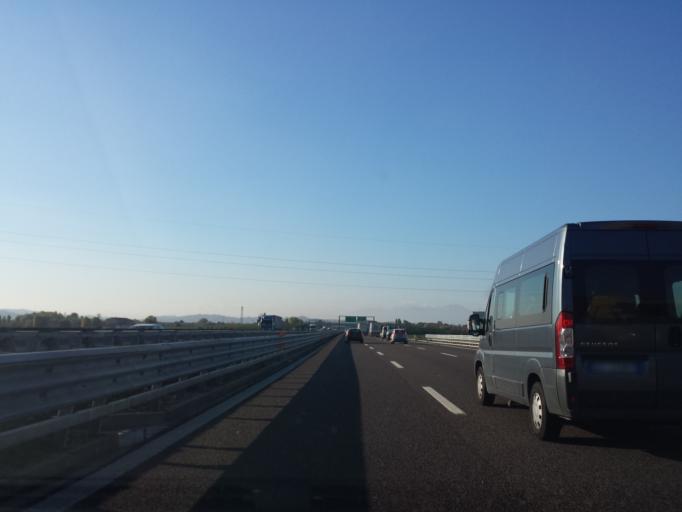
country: IT
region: Veneto
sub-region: Provincia di Vicenza
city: Torri di Quartesolo
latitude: 45.5016
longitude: 11.6358
